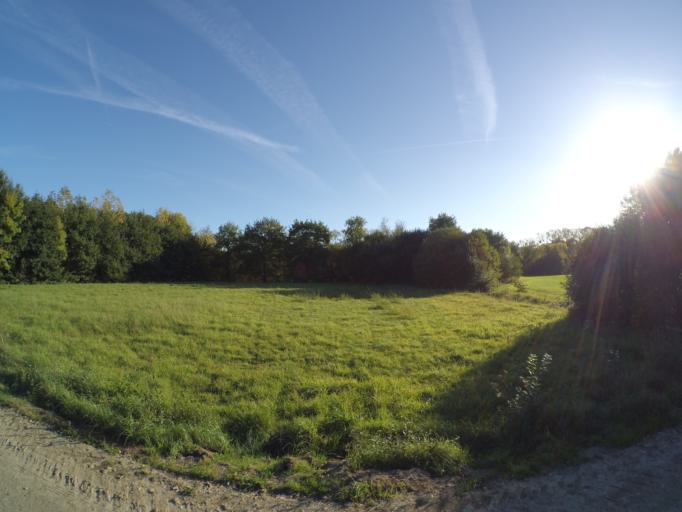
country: FR
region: Brittany
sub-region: Departement du Morbihan
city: Saint-Vincent-sur-Oust
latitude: 47.7199
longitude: -2.1523
